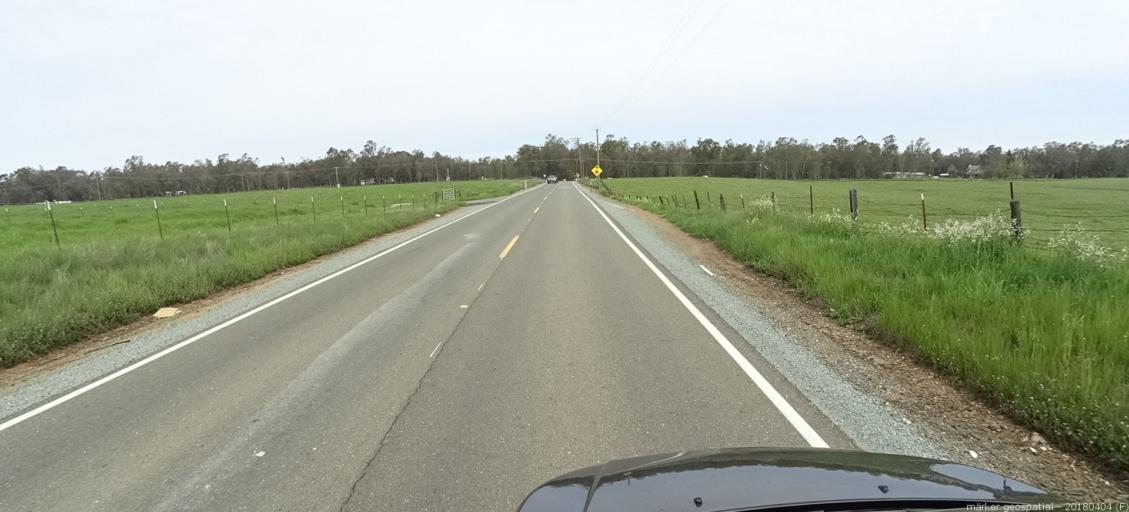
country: US
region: California
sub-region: Sacramento County
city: Clay
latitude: 38.2904
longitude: -121.1713
